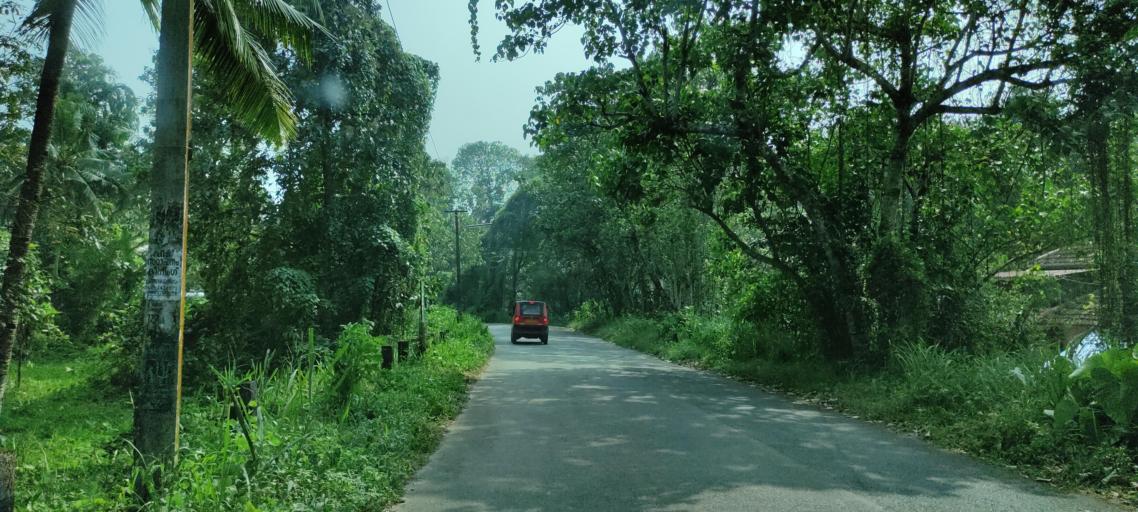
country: IN
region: Kerala
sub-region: Pattanamtitta
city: Adur
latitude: 9.2281
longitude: 76.7124
